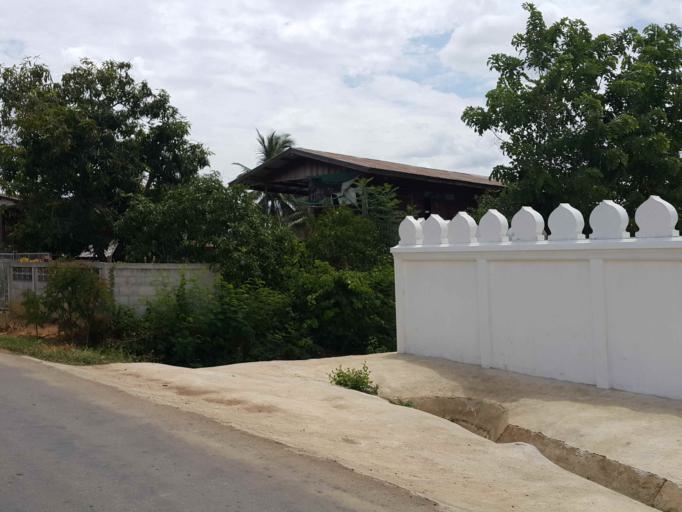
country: TH
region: Sukhothai
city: Thung Saliam
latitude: 17.3252
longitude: 99.5497
